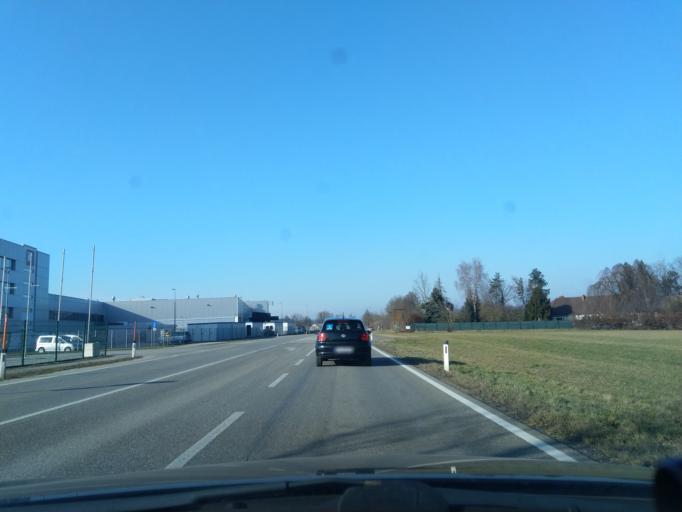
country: AT
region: Upper Austria
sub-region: Politischer Bezirk Scharding
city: Sankt Marienkirchen bei Schaerding
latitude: 48.3046
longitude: 13.4282
